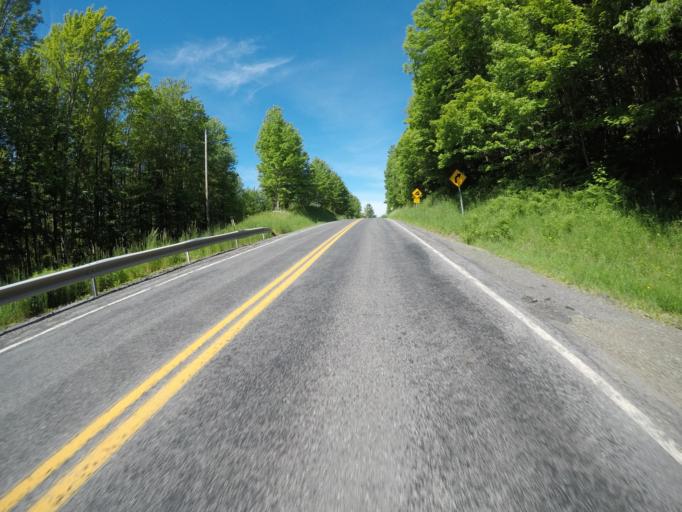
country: US
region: New York
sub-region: Delaware County
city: Delhi
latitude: 42.2122
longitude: -74.9142
